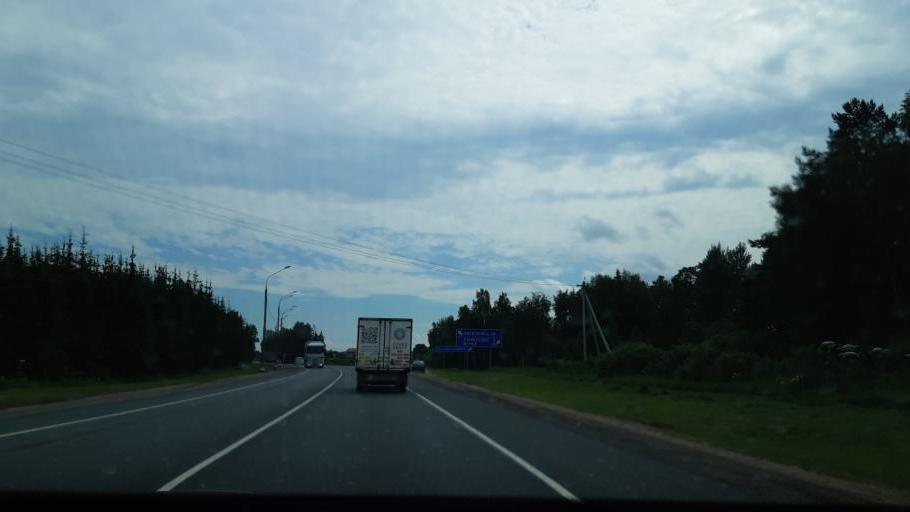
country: RU
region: Moskovskaya
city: Dorokhovo
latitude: 55.4333
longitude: 36.3519
